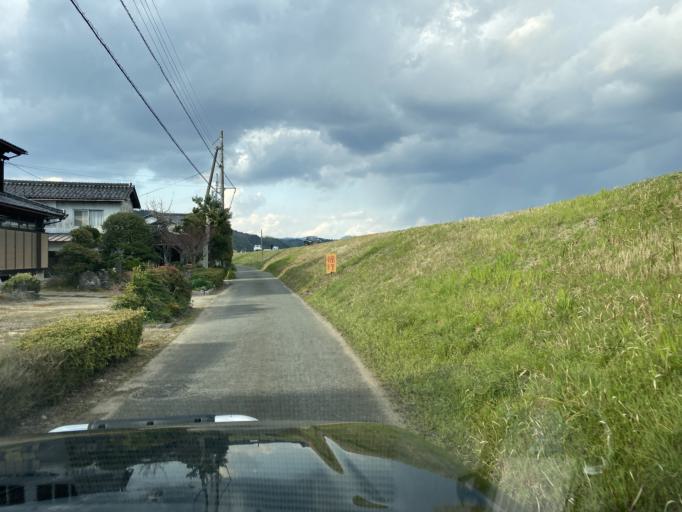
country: JP
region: Hyogo
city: Toyooka
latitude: 35.4950
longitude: 134.8075
